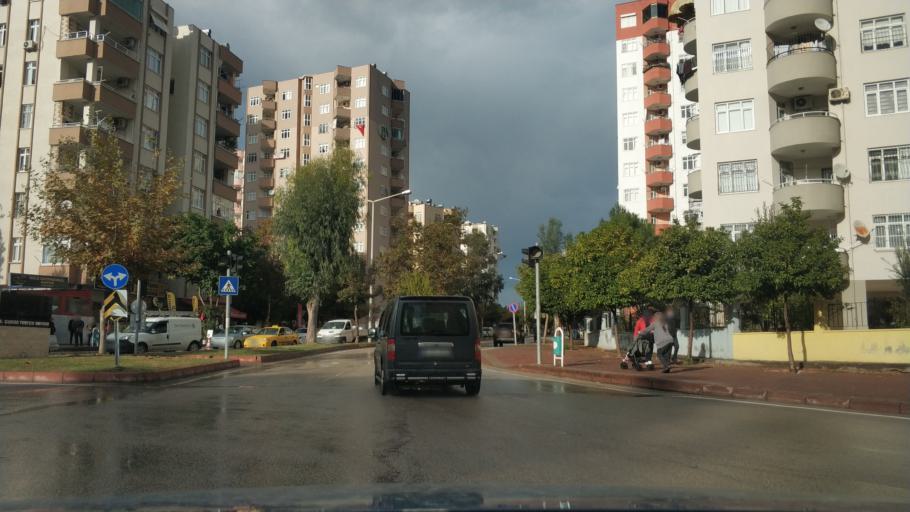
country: TR
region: Adana
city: Seyhan
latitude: 37.0349
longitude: 35.2613
